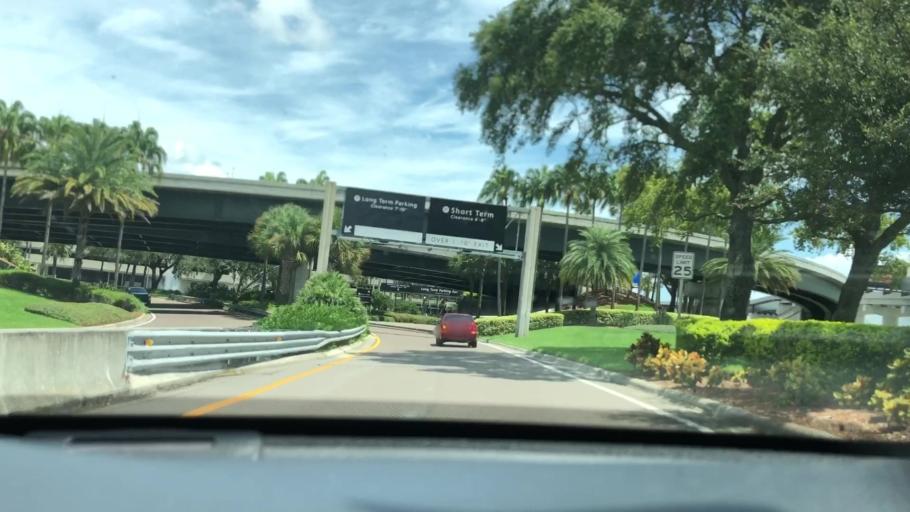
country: US
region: Florida
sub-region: Hillsborough County
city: Egypt Lake-Leto
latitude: 27.9749
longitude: -82.5351
